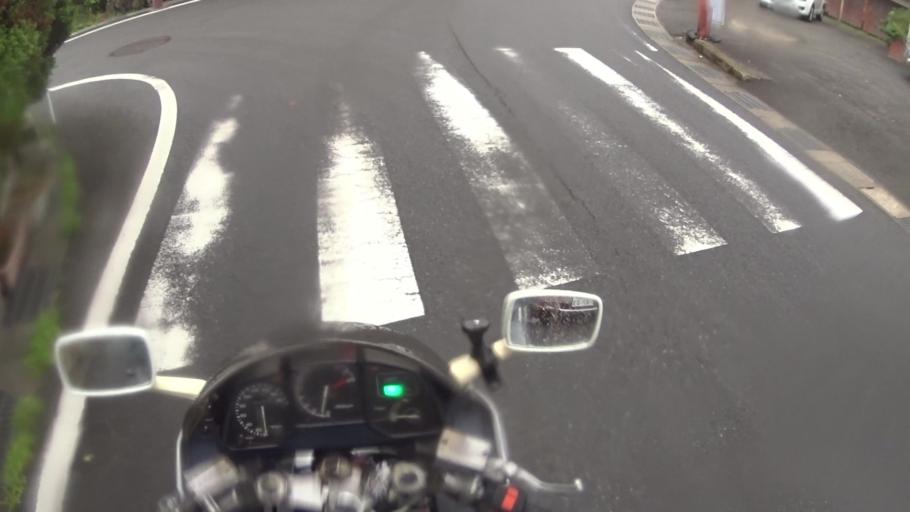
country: JP
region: Kyoto
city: Miyazu
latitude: 35.5477
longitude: 135.2351
